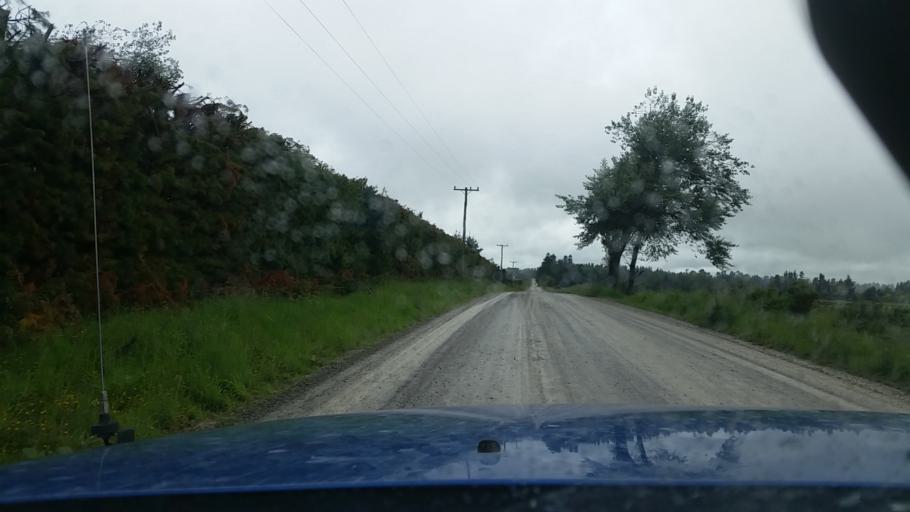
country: NZ
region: Canterbury
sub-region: Ashburton District
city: Methven
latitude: -43.6088
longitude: 171.4746
